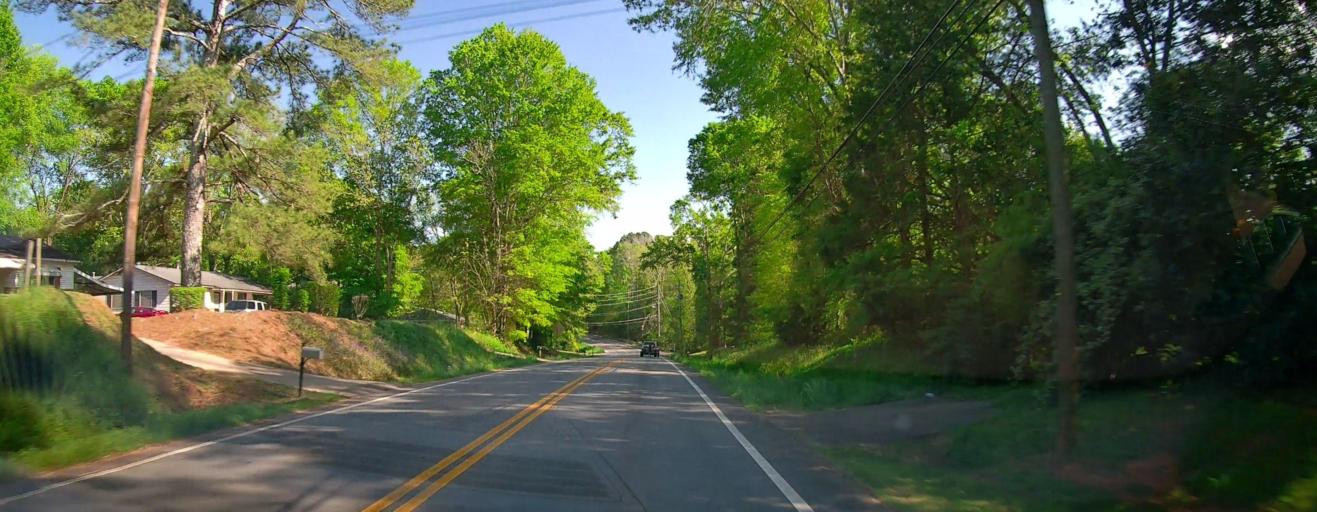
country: US
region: Georgia
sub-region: Morgan County
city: Madison
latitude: 33.6027
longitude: -83.4750
